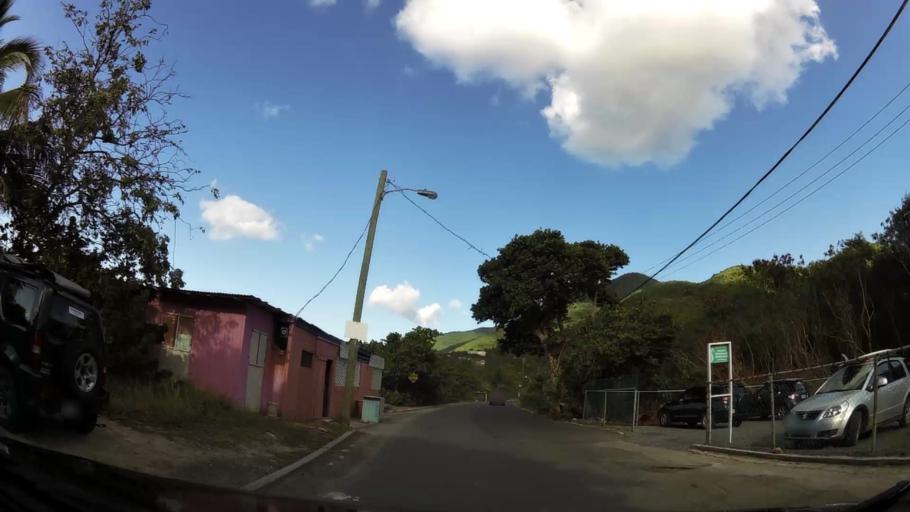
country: VG
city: Road Town
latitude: 18.3988
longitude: -64.6818
